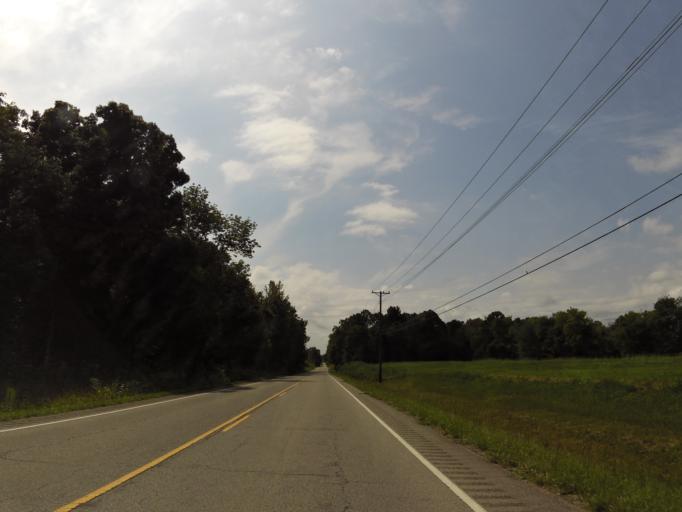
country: US
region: Tennessee
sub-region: Humphreys County
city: Waverly
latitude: 35.8625
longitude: -87.8095
